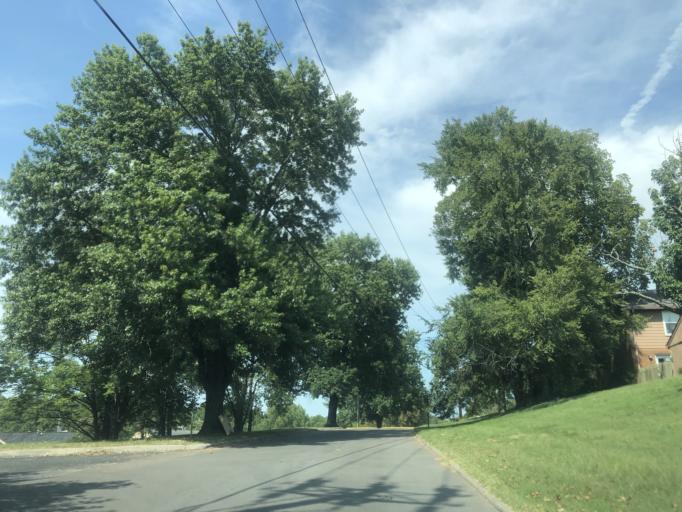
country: US
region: Tennessee
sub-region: Williamson County
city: Brentwood Estates
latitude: 36.0461
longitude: -86.7064
